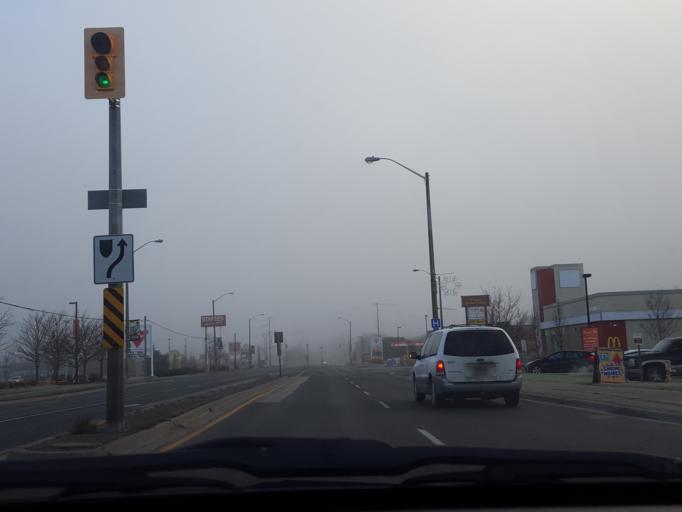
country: CA
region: Ontario
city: Angus
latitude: 44.1475
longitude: -79.8855
